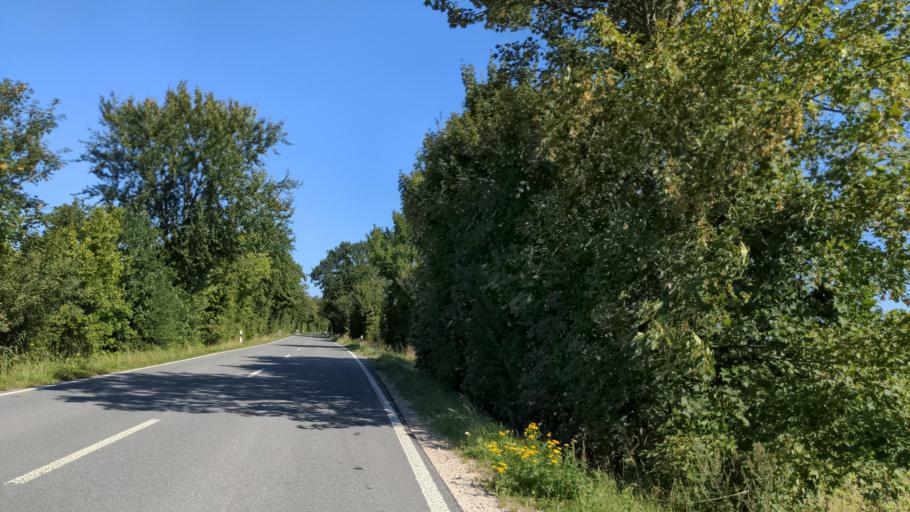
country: DE
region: Schleswig-Holstein
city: Grinau
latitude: 53.7858
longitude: 10.5590
